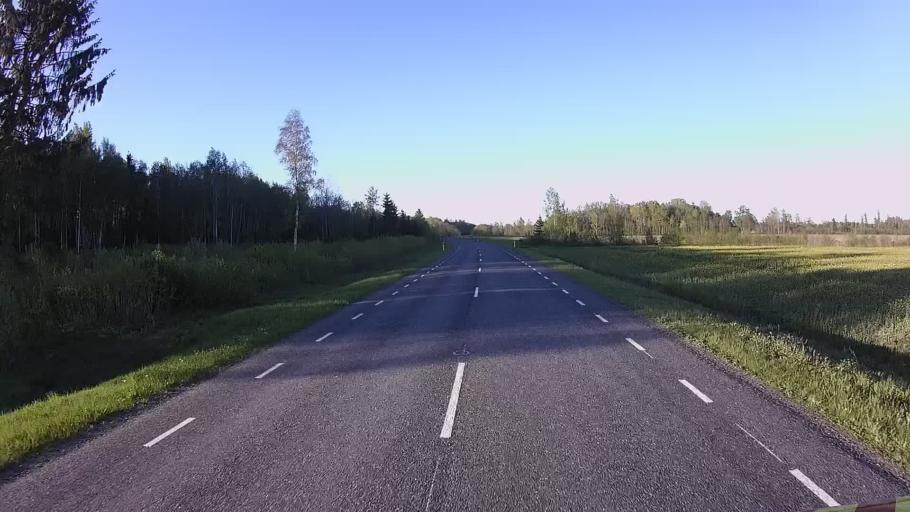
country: EE
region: Jogevamaa
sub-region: Poltsamaa linn
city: Poltsamaa
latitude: 58.5064
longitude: 25.8435
